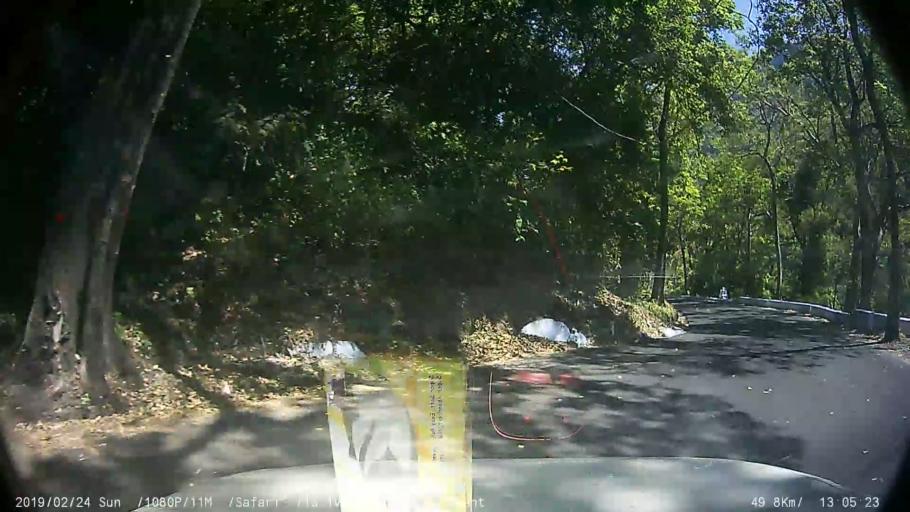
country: IN
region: Tamil Nadu
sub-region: Nilgiri
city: Wellington
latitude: 11.3343
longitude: 76.8266
